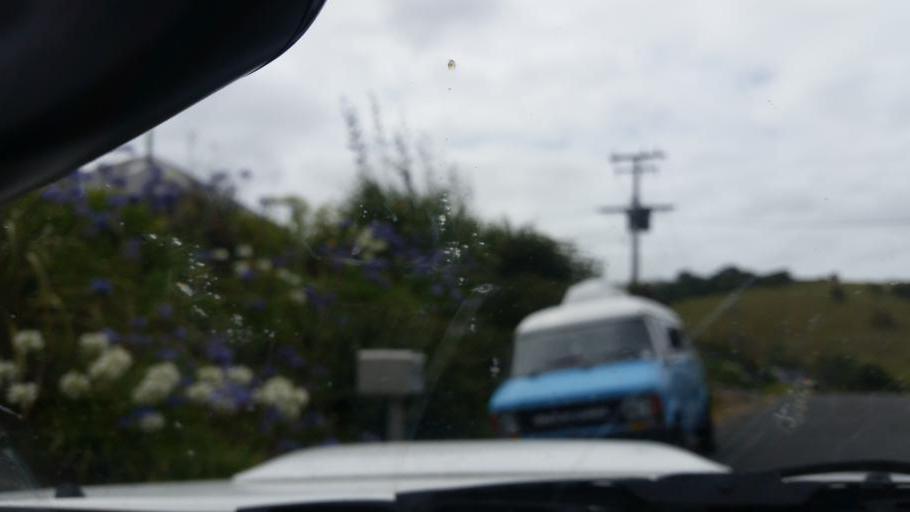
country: NZ
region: Auckland
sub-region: Auckland
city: Wellsford
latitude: -36.1562
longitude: 174.2369
